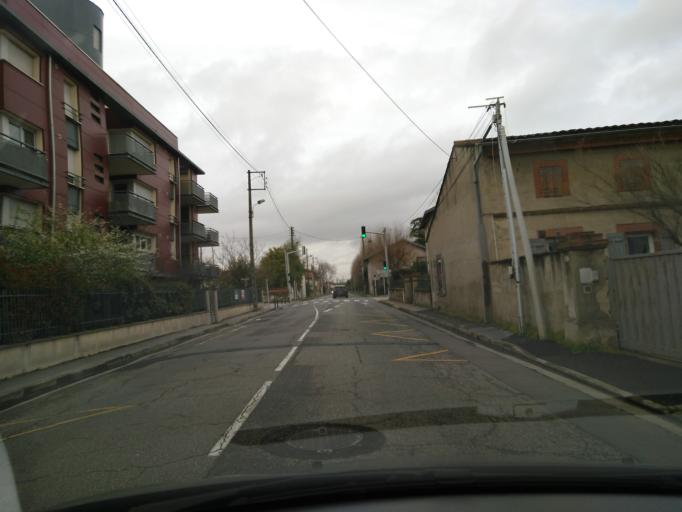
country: FR
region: Midi-Pyrenees
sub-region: Departement de la Haute-Garonne
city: Toulouse
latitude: 43.6307
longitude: 1.4380
